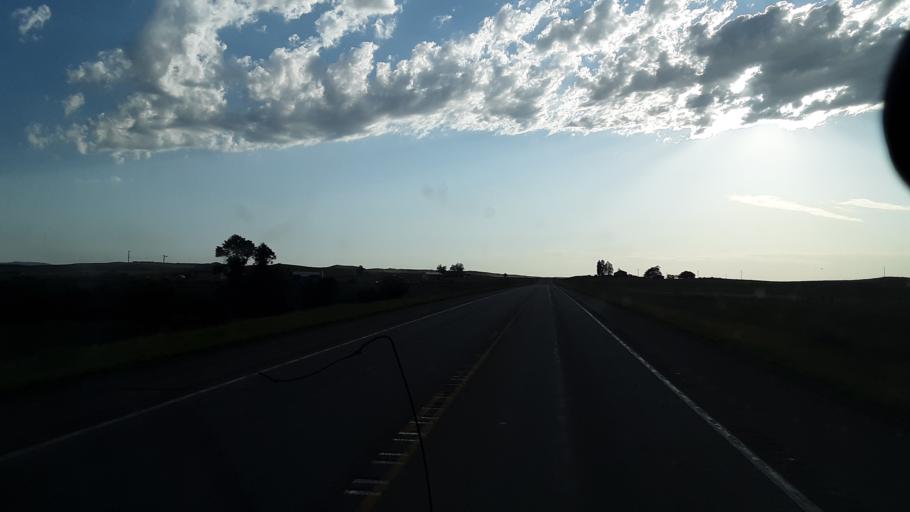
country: US
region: Montana
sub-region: Rosebud County
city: Lame Deer
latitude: 45.5285
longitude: -106.9704
